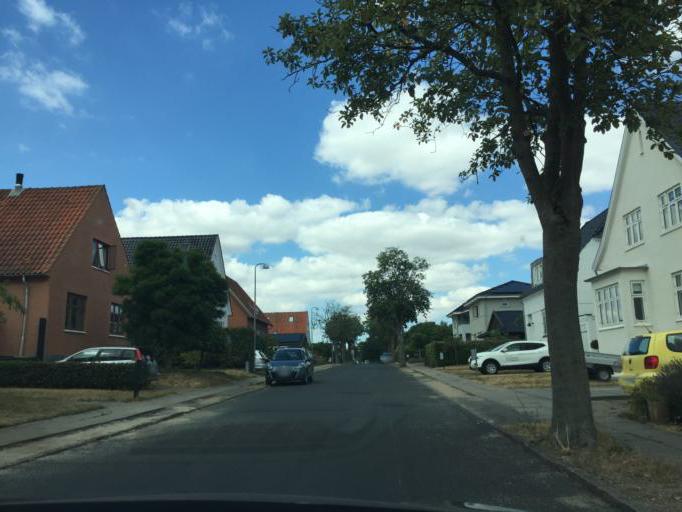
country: DK
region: South Denmark
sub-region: Odense Kommune
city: Odense
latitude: 55.4080
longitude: 10.3481
